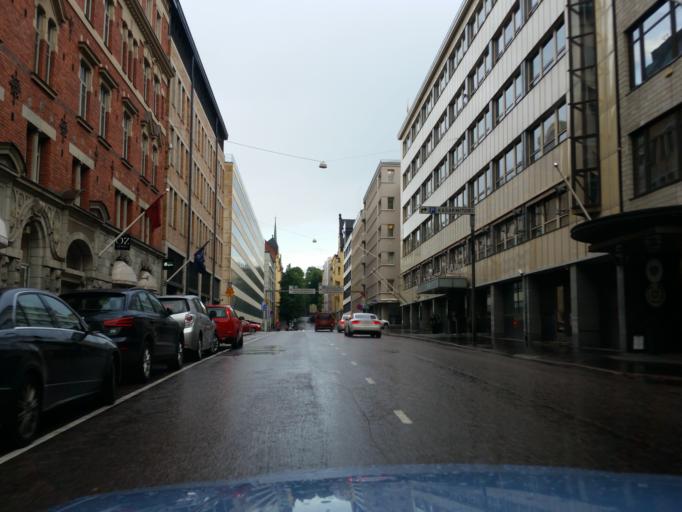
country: FI
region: Uusimaa
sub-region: Helsinki
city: Helsinki
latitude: 60.1664
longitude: 24.9513
